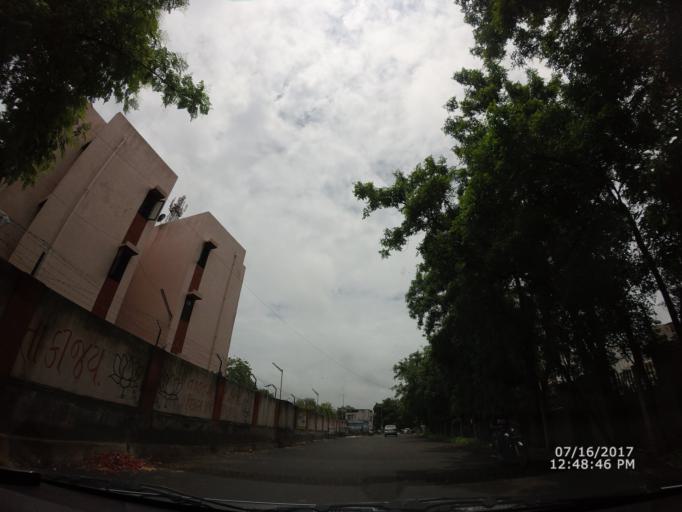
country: IN
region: Gujarat
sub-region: Ahmadabad
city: Sarkhej
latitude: 23.0179
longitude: 72.5085
